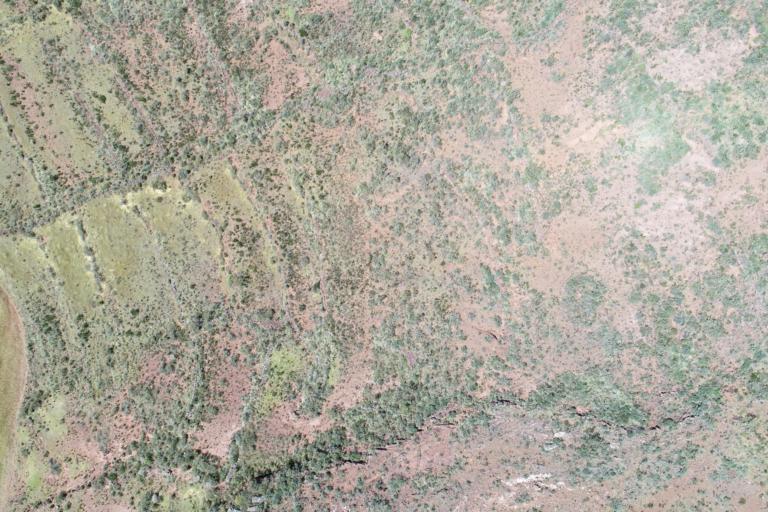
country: BO
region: La Paz
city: Tiahuanaco
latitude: -16.6041
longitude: -68.7705
